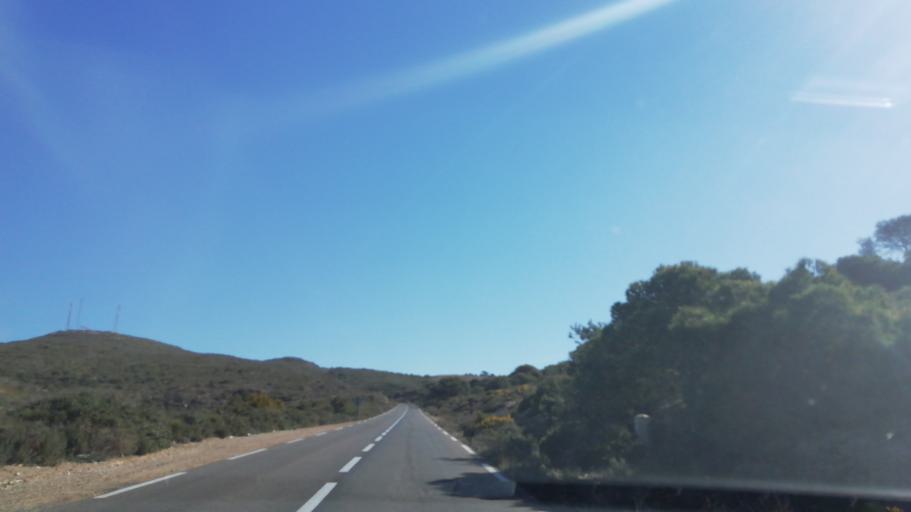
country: DZ
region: Ain Temouchent
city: El Amria
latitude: 35.6479
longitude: -1.0445
